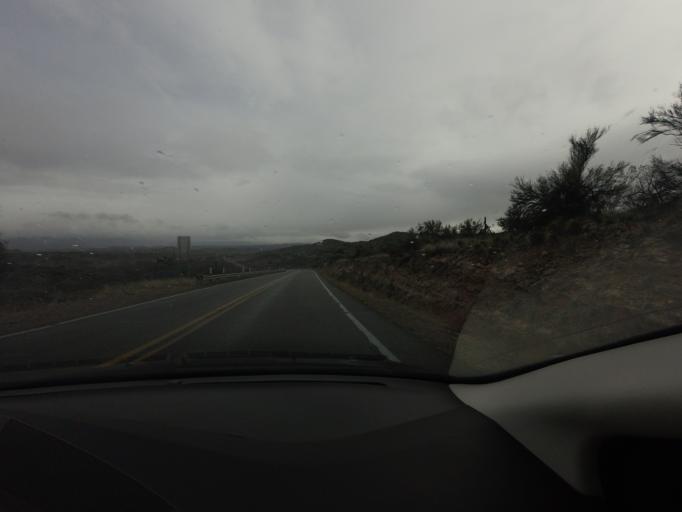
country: US
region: Arizona
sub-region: Yavapai County
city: Lake Montezuma
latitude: 34.6730
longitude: -111.8354
